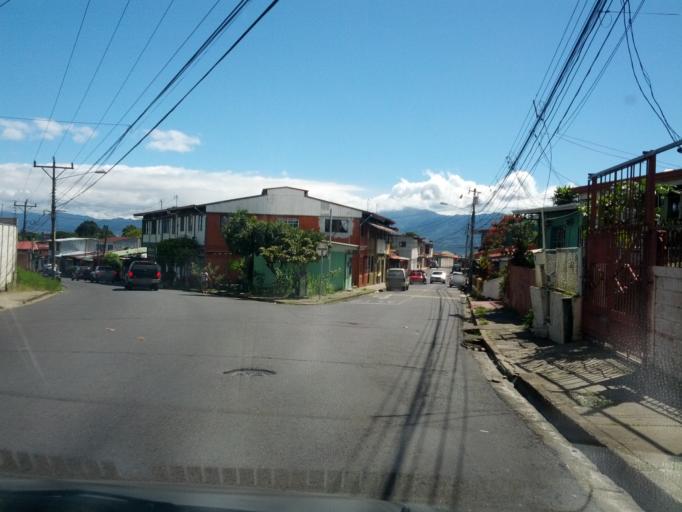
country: CR
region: Alajuela
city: Alajuela
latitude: 10.0215
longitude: -84.2009
